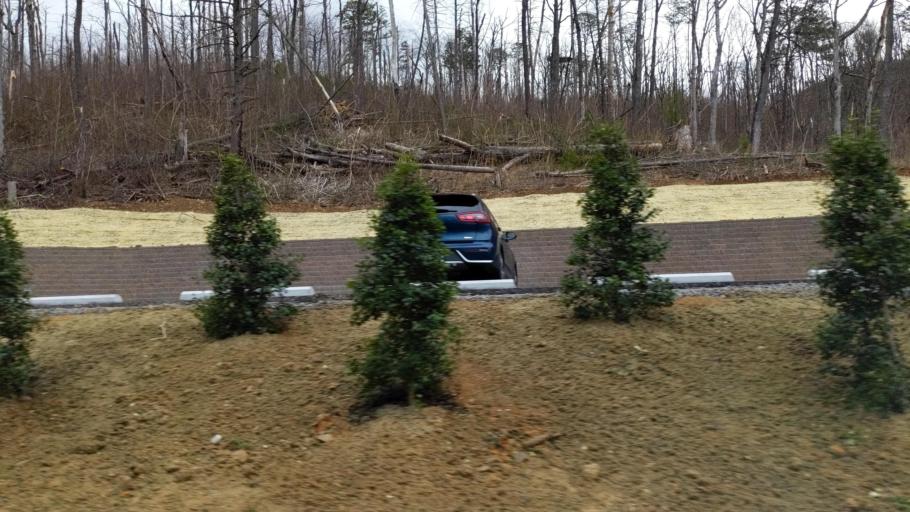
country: US
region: Tennessee
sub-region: Sevier County
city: Gatlinburg
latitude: 35.7134
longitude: -83.5076
